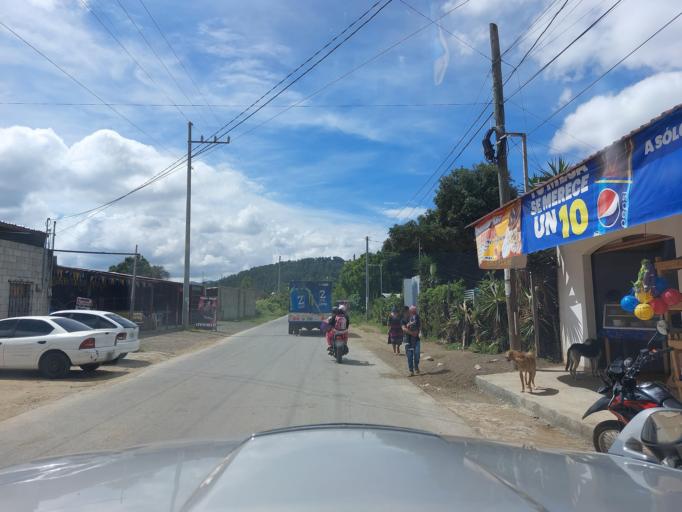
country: GT
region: Chimaltenango
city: San Andres Itzapa
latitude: 14.6197
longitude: -90.8342
